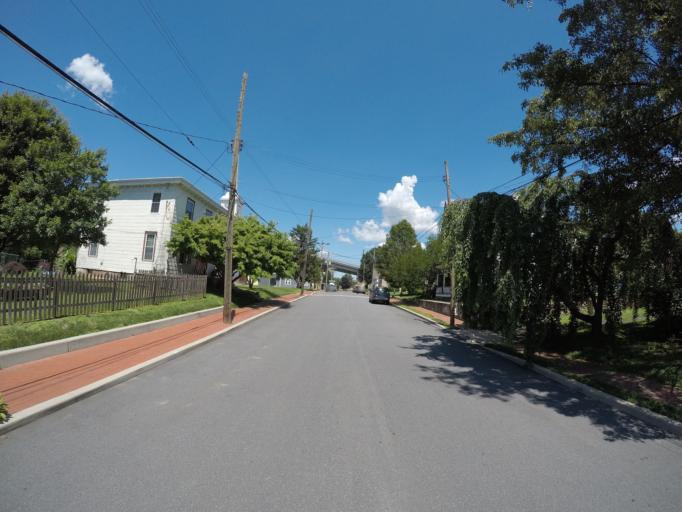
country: US
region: Delaware
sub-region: New Castle County
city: Delaware City
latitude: 39.5558
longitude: -75.6515
